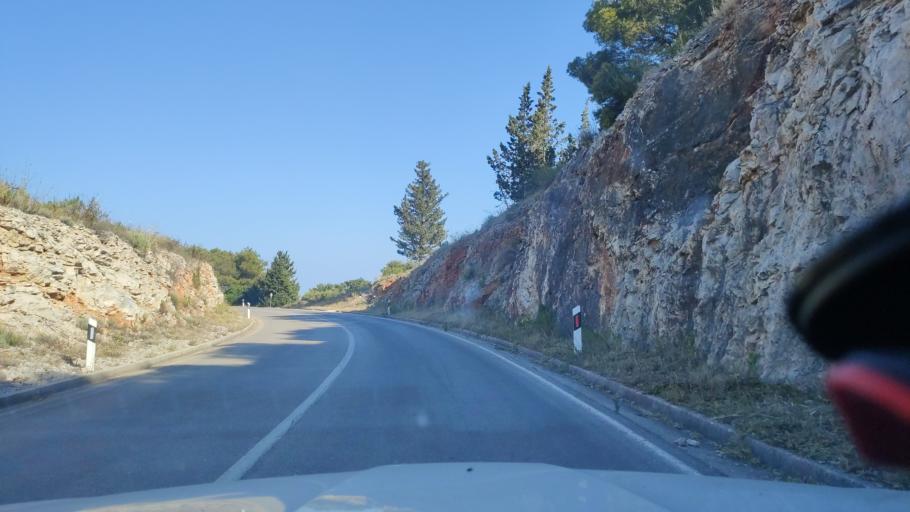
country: HR
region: Splitsko-Dalmatinska
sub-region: Grad Vis
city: Vis
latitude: 43.0323
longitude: 16.2023
